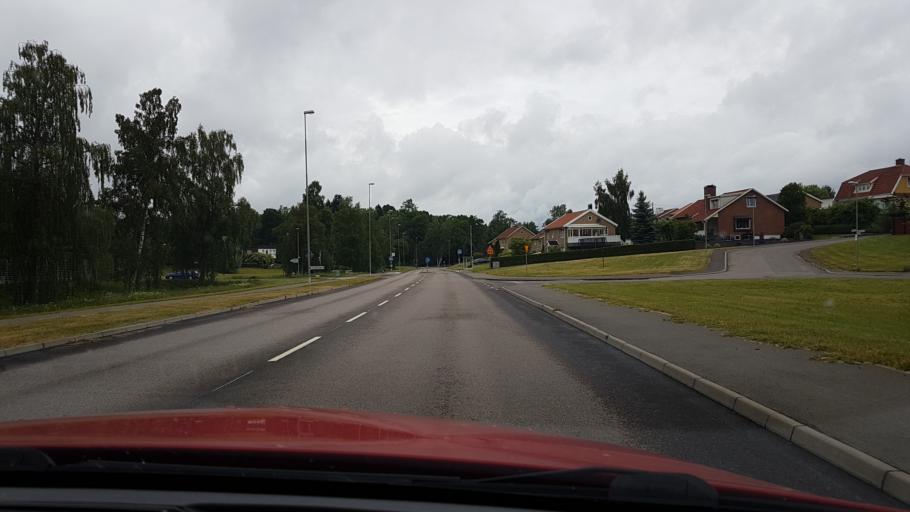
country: SE
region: Vaestra Goetaland
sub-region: Skovde Kommun
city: Skultorp
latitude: 58.3730
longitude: 13.8300
